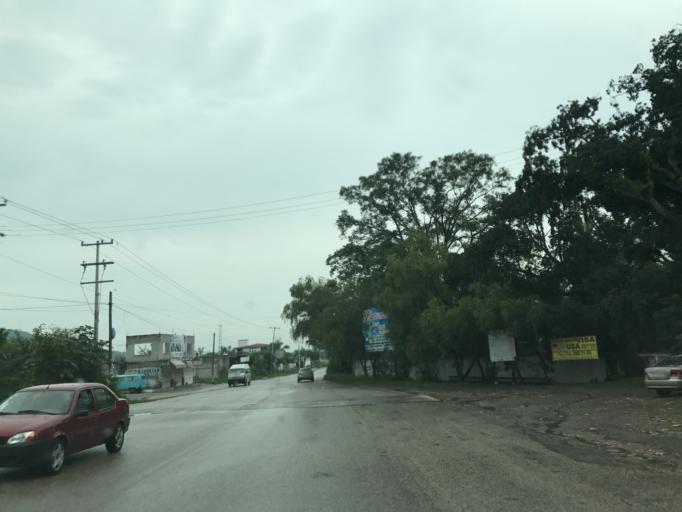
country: MX
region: Morelos
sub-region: Ayala
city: Ciudad Ayala
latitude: 18.7551
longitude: -98.9850
